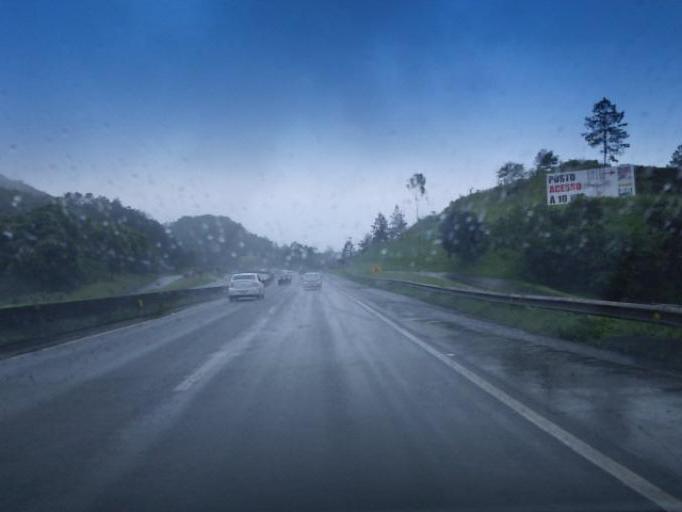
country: BR
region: Santa Catarina
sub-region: Joinville
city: Joinville
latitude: -26.1403
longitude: -48.9024
